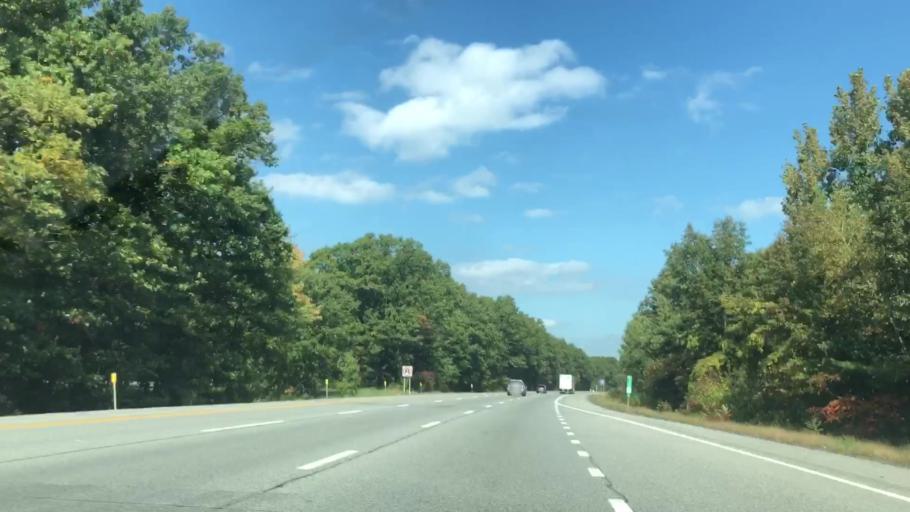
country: US
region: New York
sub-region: Saratoga County
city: Saratoga Springs
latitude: 43.1017
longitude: -73.7528
